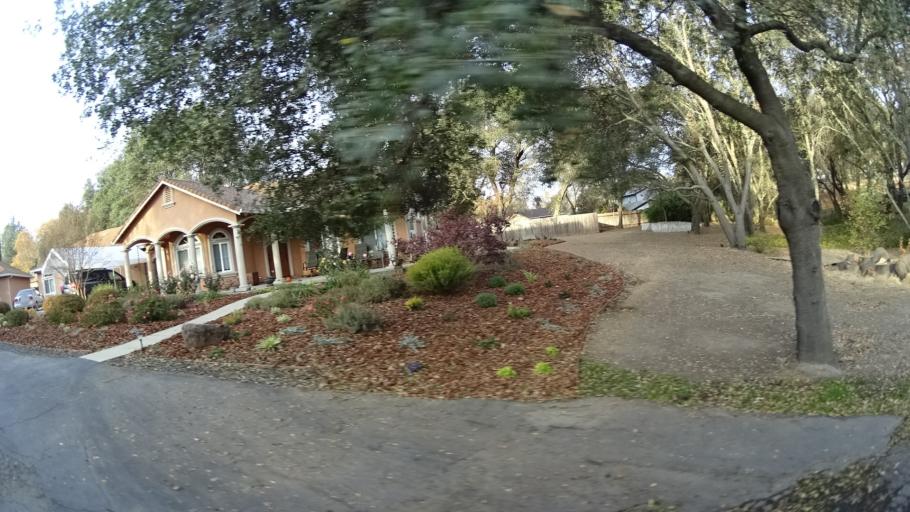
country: US
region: California
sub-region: Sacramento County
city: Citrus Heights
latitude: 38.7168
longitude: -121.2755
